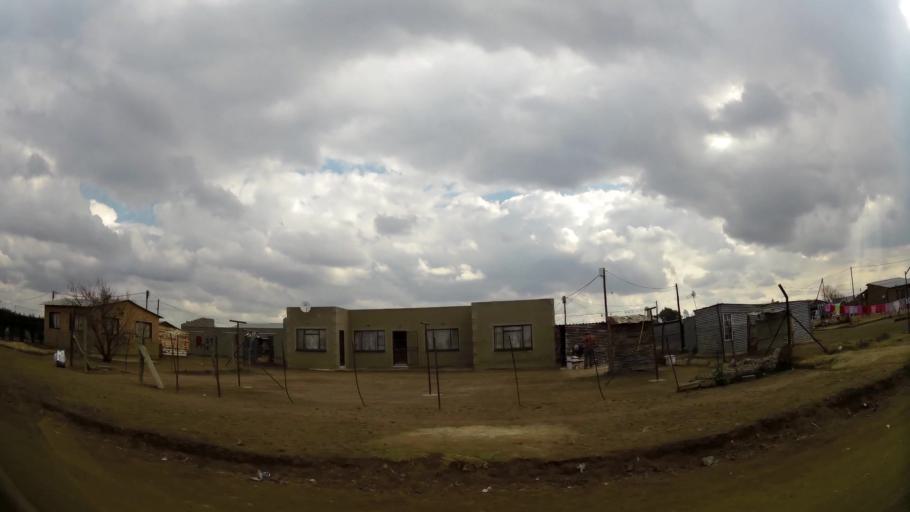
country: ZA
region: Orange Free State
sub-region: Fezile Dabi District Municipality
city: Sasolburg
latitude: -26.8533
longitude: 27.8925
